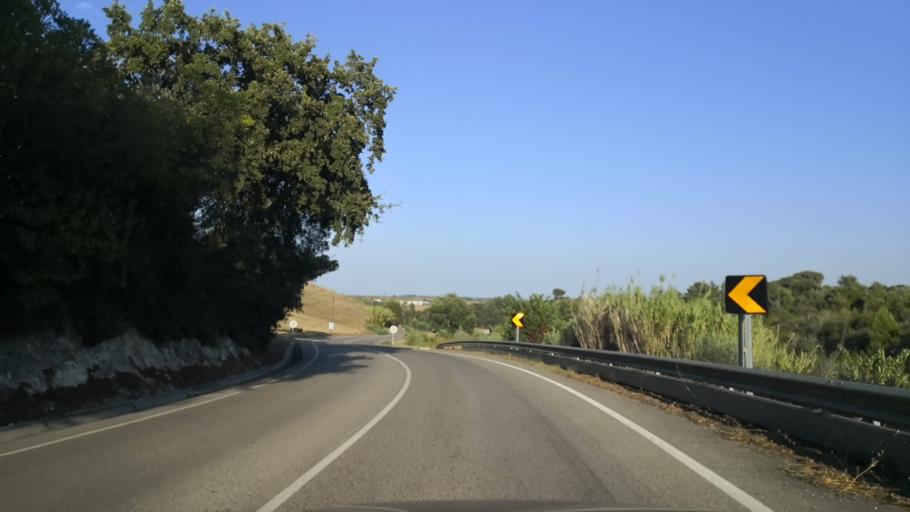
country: PT
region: Santarem
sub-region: Alcanena
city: Alcanena
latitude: 39.3557
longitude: -8.6602
